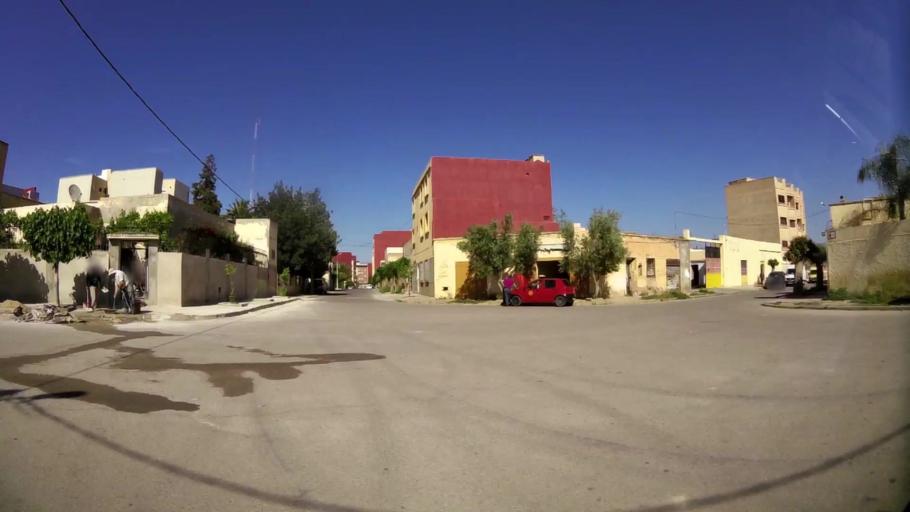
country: MA
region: Oriental
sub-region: Oujda-Angad
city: Oujda
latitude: 34.6878
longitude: -1.9220
